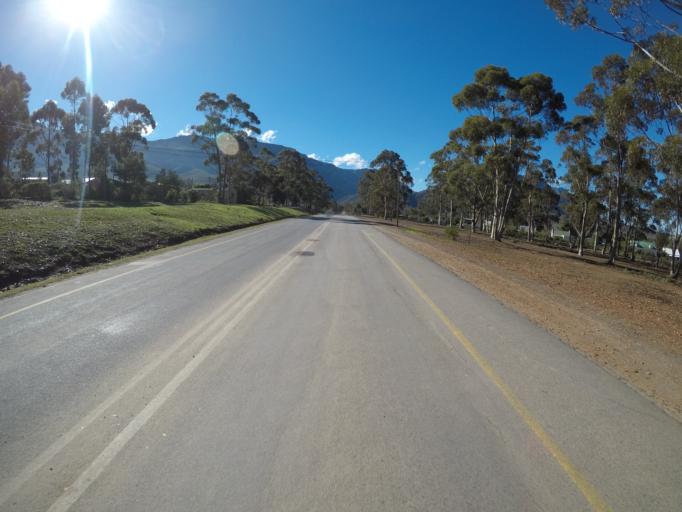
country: ZA
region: Western Cape
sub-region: Overberg District Municipality
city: Caledon
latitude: -34.0551
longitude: 19.6017
